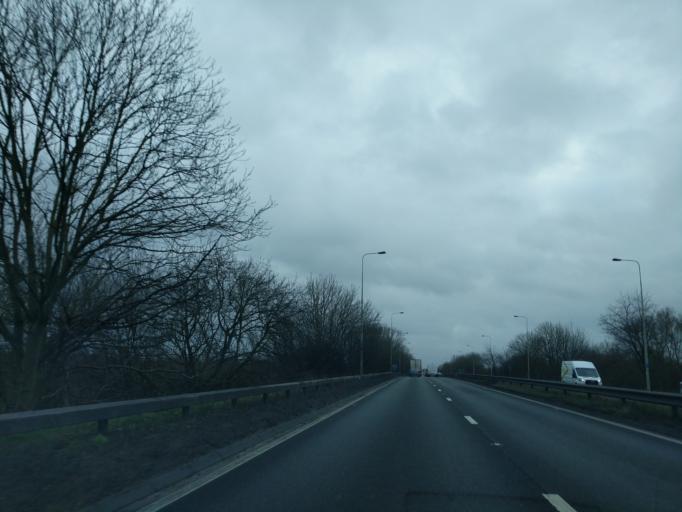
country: GB
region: England
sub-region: Staffordshire
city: Barton under Needwood
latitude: 52.7409
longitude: -1.7284
